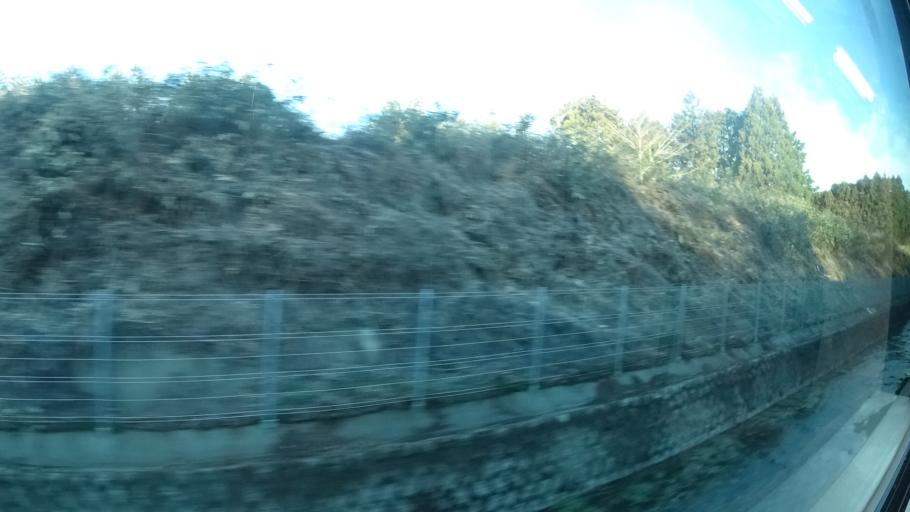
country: JP
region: Fukushima
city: Namie
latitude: 37.3994
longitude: 140.9861
